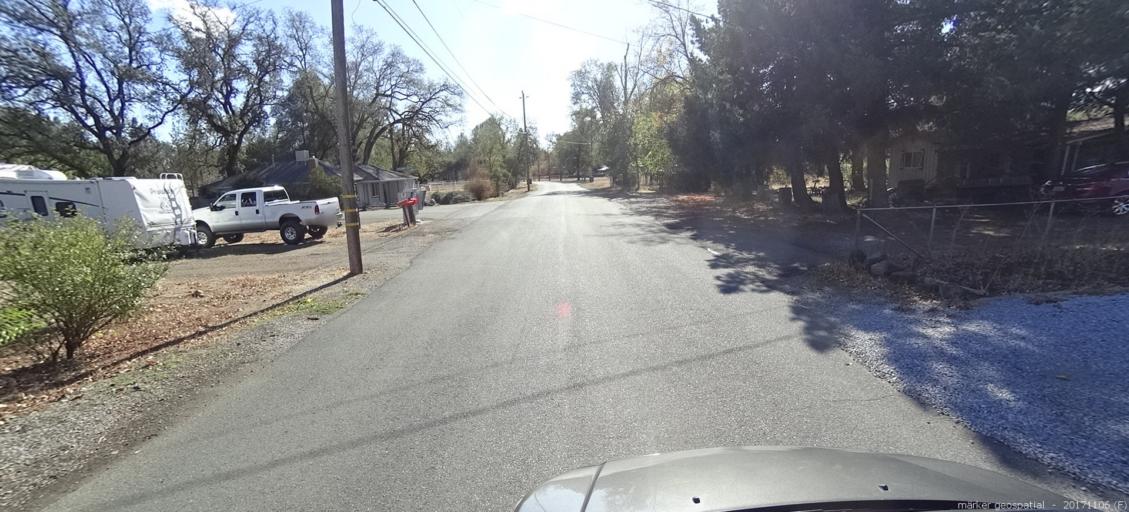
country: US
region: California
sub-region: Shasta County
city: Palo Cedro
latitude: 40.5865
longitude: -122.2969
